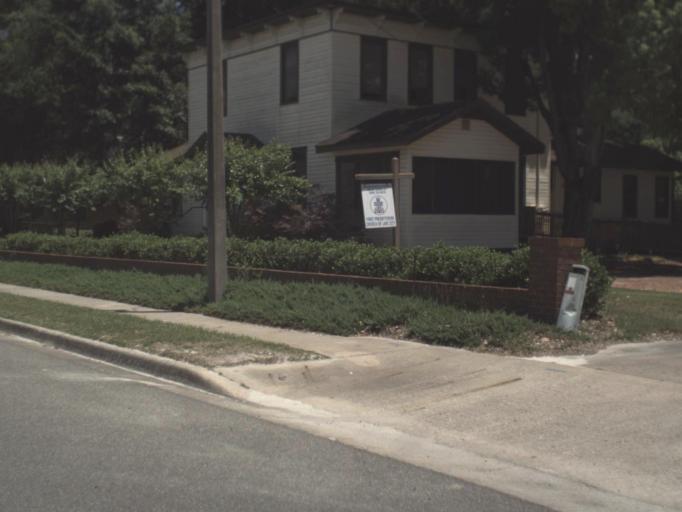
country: US
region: Florida
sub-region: Columbia County
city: Lake City
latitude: 30.1892
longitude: -82.6459
